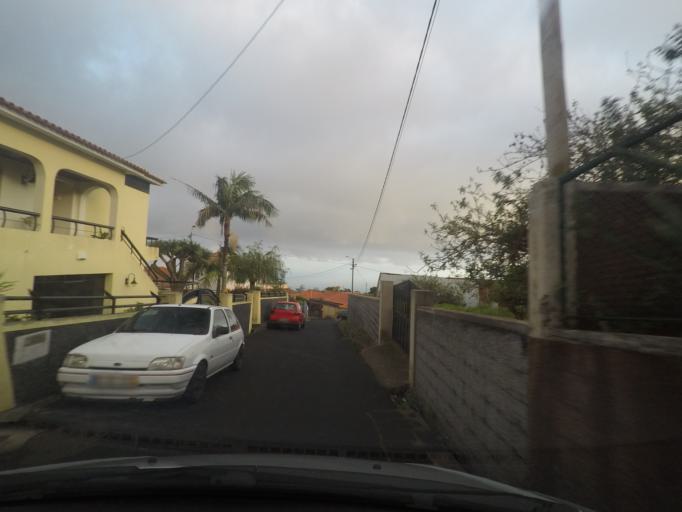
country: PT
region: Madeira
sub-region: Santa Cruz
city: Camacha
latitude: 32.6804
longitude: -16.8518
